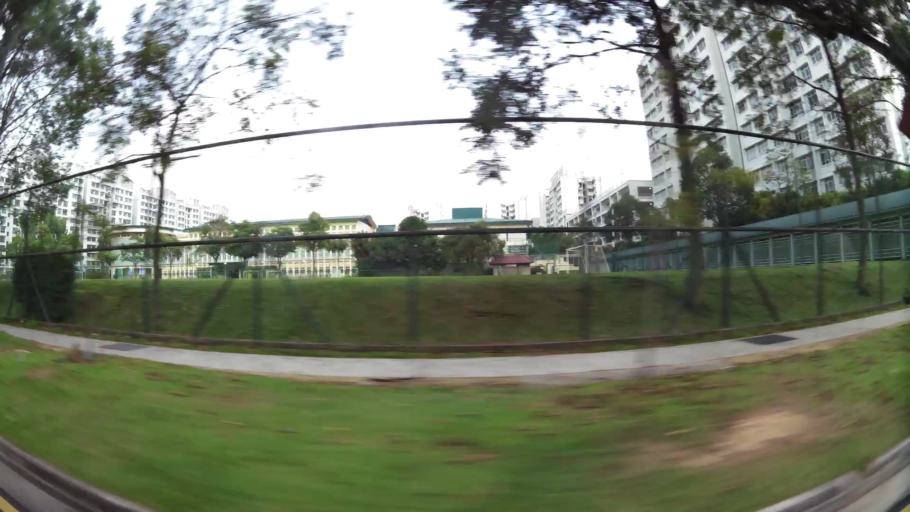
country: MY
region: Johor
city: Kampung Pasir Gudang Baru
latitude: 1.4207
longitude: 103.8439
